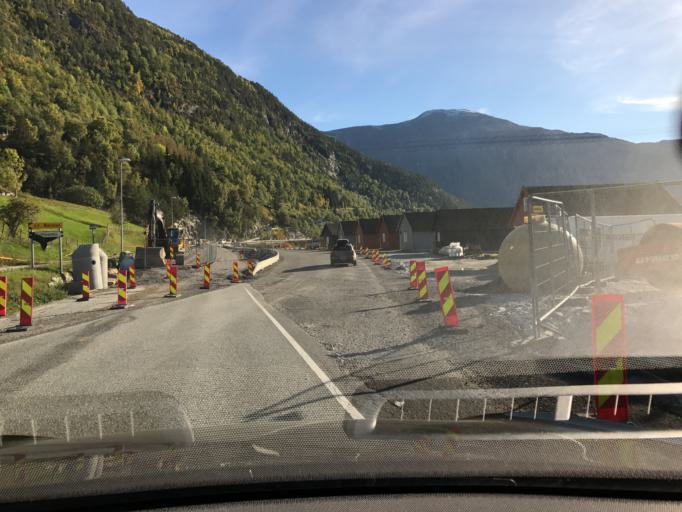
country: NO
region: Sogn og Fjordane
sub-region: Sogndal
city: Sogndalsfjora
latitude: 61.2304
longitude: 7.1236
